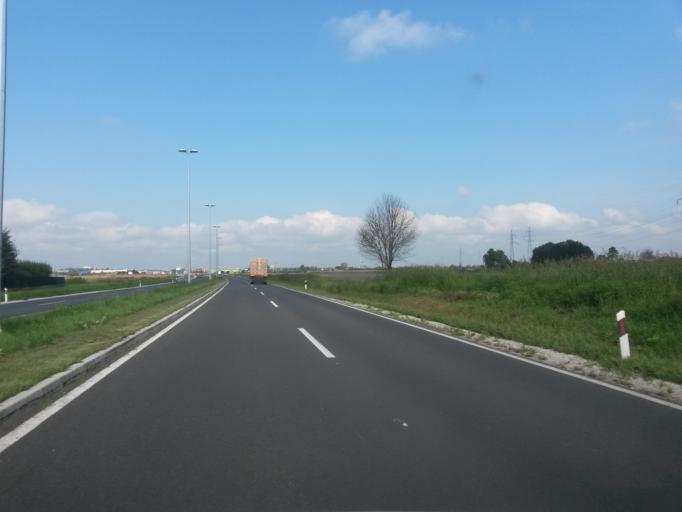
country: HR
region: Varazdinska
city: Varazdin
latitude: 46.2763
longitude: 16.3608
